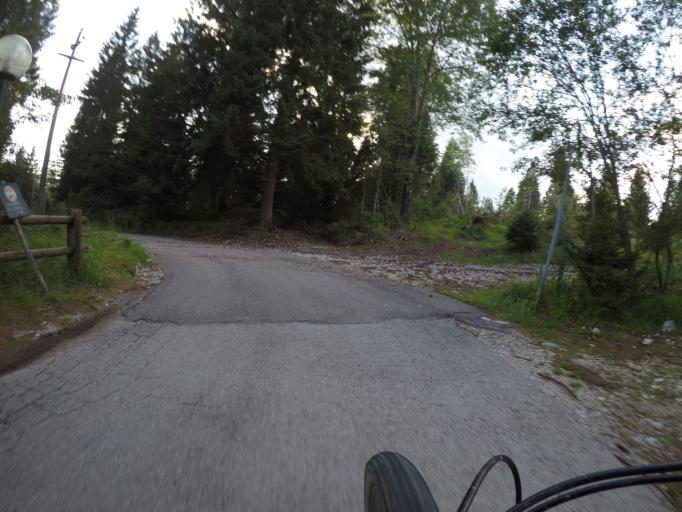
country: IT
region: Veneto
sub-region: Provincia di Vicenza
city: Gallio
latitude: 45.8881
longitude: 11.5306
